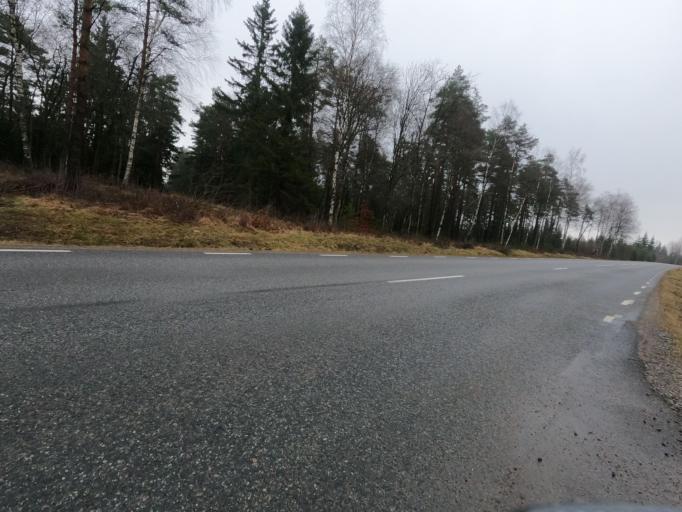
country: SE
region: Halland
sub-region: Hylte Kommun
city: Hyltebruk
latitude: 56.8247
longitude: 13.4091
